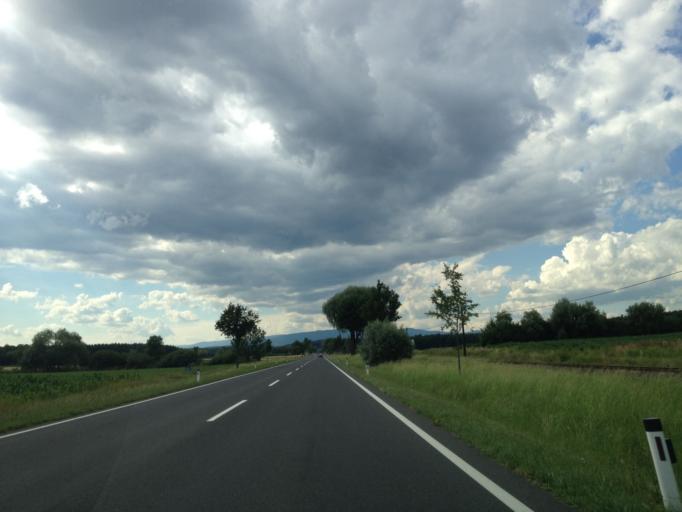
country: AT
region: Burgenland
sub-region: Politischer Bezirk Oberwart
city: Oberwart
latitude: 47.3161
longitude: 16.1829
